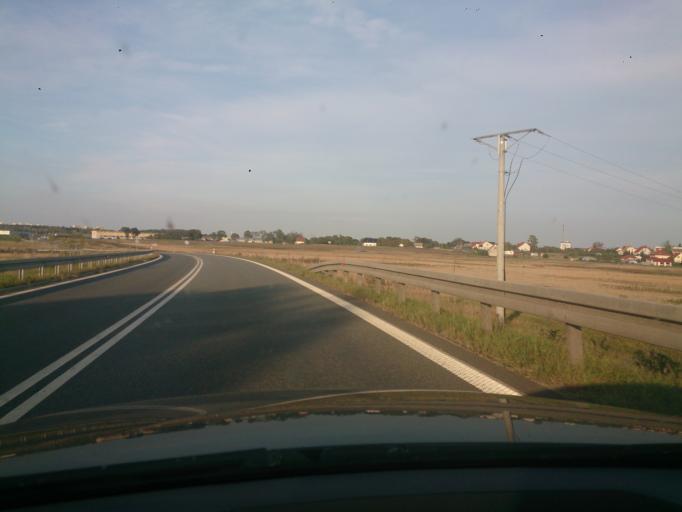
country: PL
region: Kujawsko-Pomorskie
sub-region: Grudziadz
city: Grudziadz
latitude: 53.4308
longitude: 18.7066
